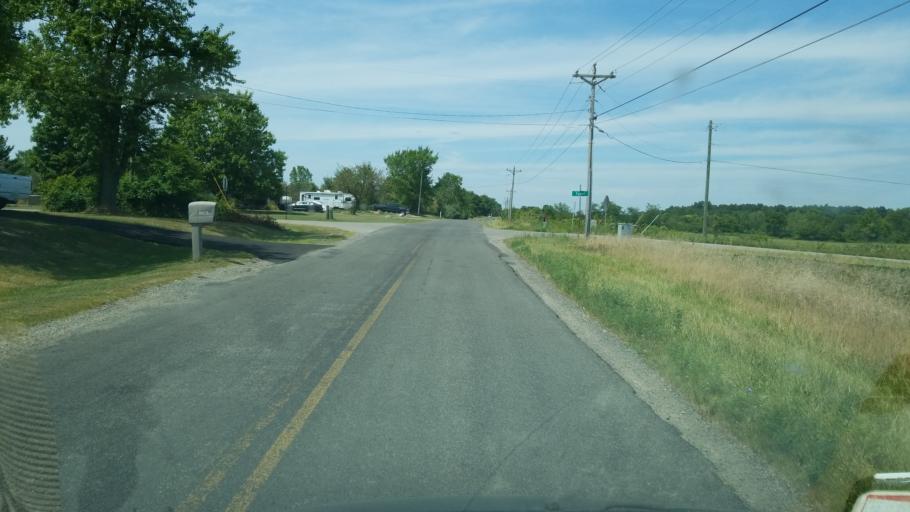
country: US
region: Ohio
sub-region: Union County
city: New California
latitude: 40.1543
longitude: -83.2625
